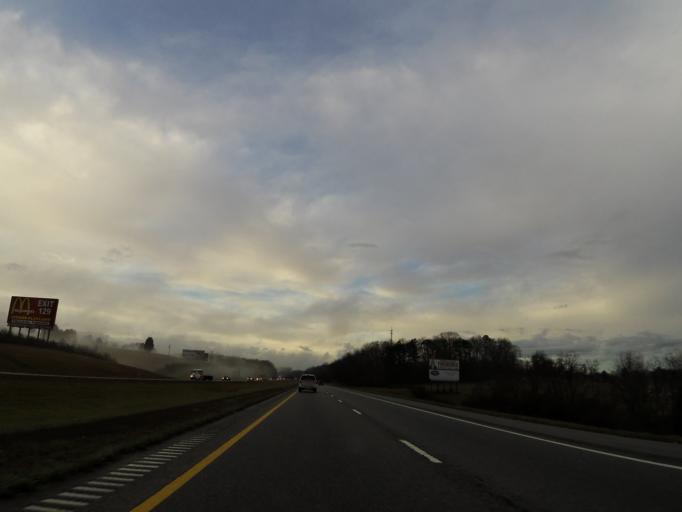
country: US
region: Tennessee
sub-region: Anderson County
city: Norris
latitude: 36.1808
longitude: -84.0936
